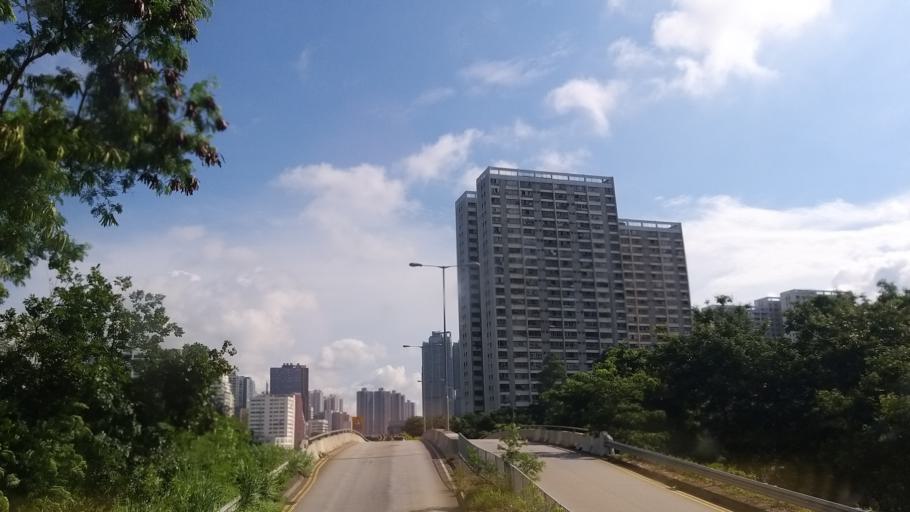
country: HK
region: Tuen Mun
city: Tuen Mun
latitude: 22.3855
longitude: 113.9709
